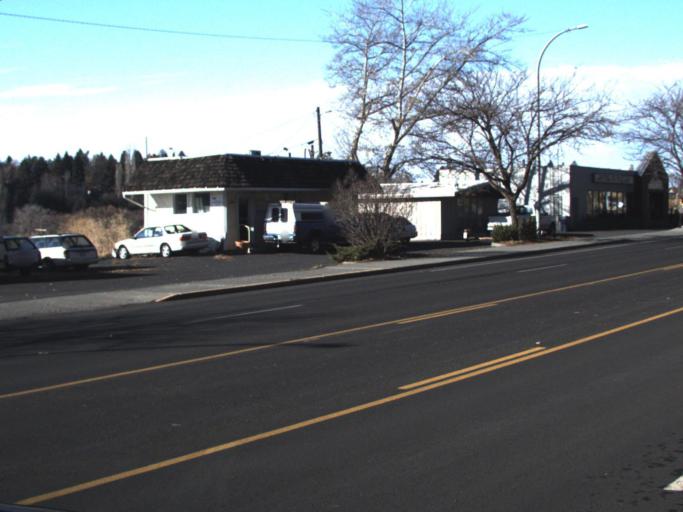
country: US
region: Washington
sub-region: Whitman County
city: Pullman
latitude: 46.7252
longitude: -117.1663
